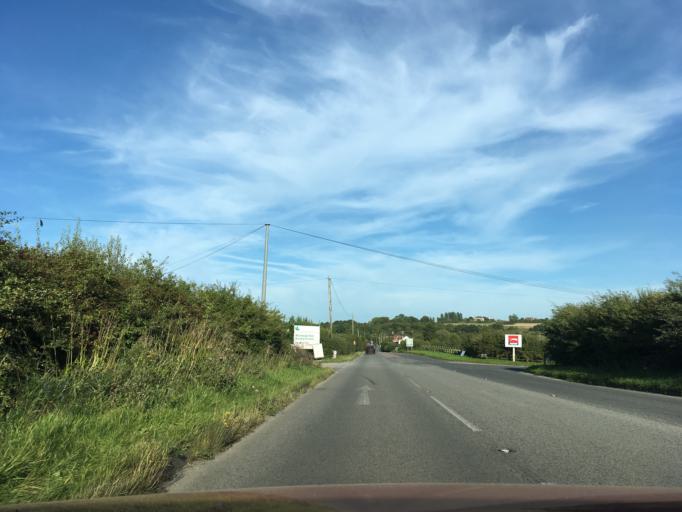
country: GB
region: England
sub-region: South Gloucestershire
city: Pucklechurch
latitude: 51.5104
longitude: -2.4504
